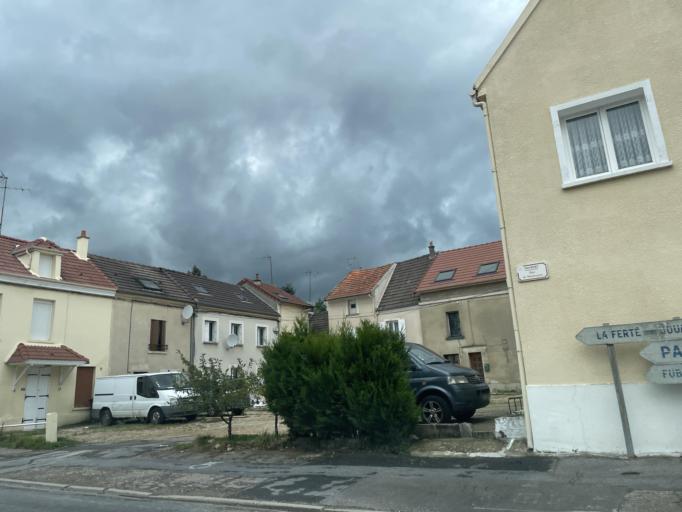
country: FR
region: Ile-de-France
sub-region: Departement de Seine-et-Marne
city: Trilport
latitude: 48.9564
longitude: 2.9507
